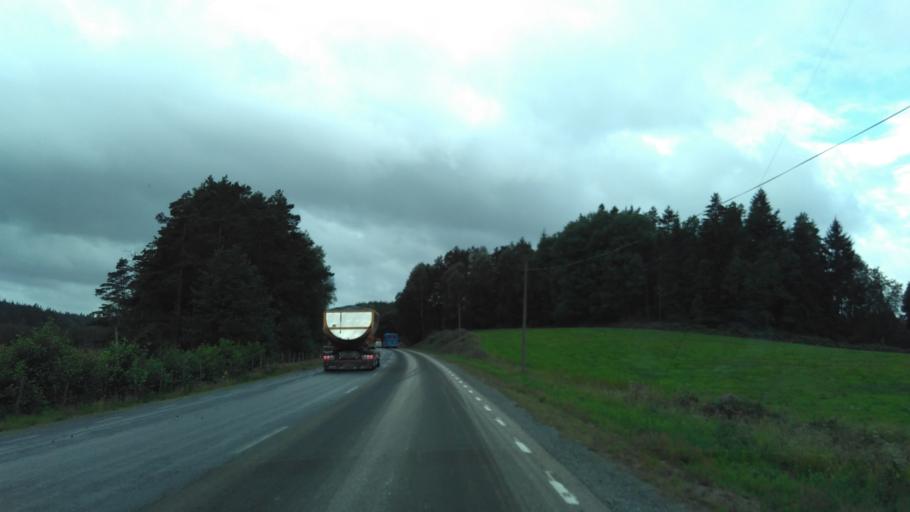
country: SE
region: Vaestra Goetaland
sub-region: Marks Kommun
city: Fritsla
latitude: 57.5677
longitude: 12.8203
